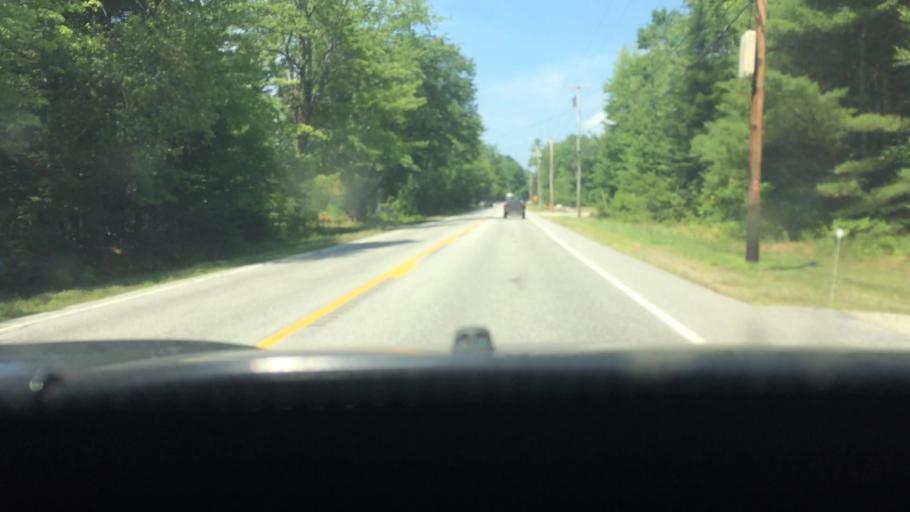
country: US
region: Maine
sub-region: Androscoggin County
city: Minot
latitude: 44.0940
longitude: -70.3513
